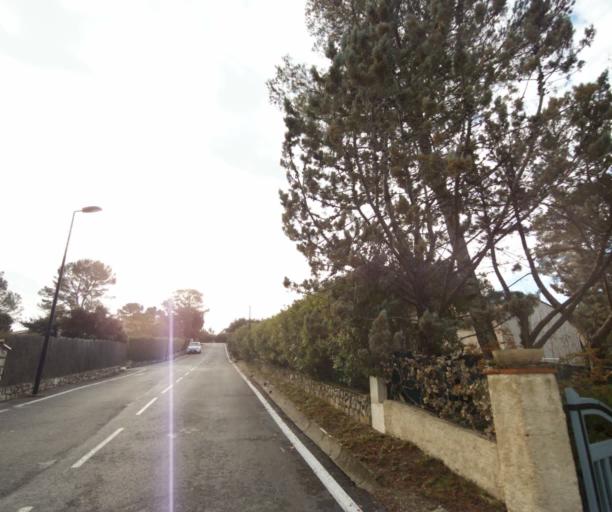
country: FR
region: Provence-Alpes-Cote d'Azur
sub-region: Departement du Var
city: Trans-en-Provence
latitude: 43.4918
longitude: 6.4965
